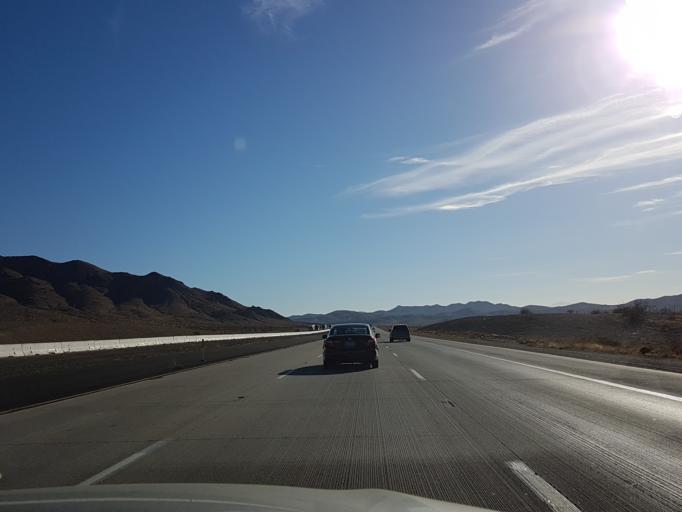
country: US
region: California
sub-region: San Bernardino County
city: Lenwood
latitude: 34.7396
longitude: -117.1791
